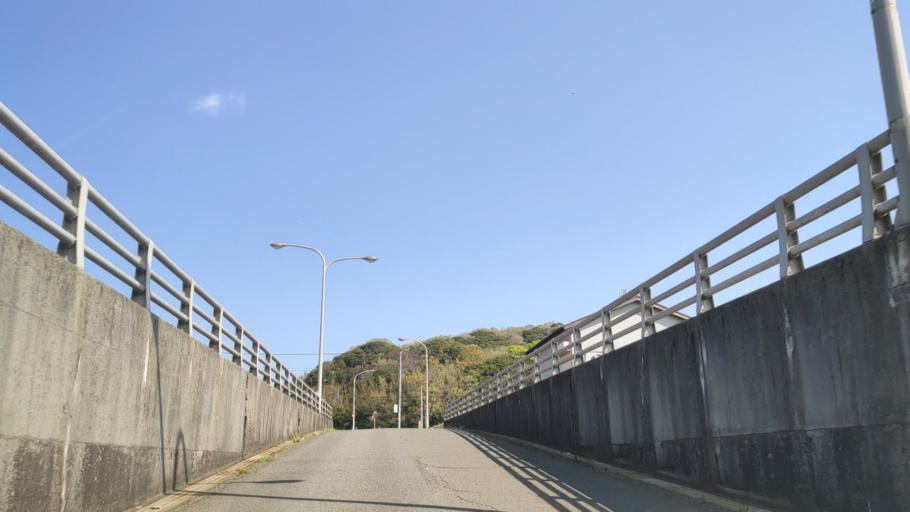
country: JP
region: Kanagawa
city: Oiso
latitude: 35.3084
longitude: 139.2967
